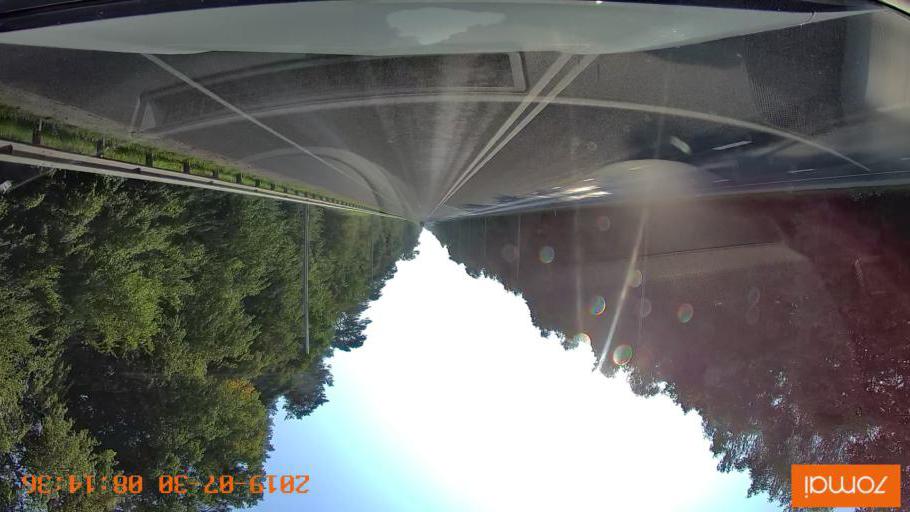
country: RU
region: Kaliningrad
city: Zheleznodorozhnyy
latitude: 54.6473
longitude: 21.3616
